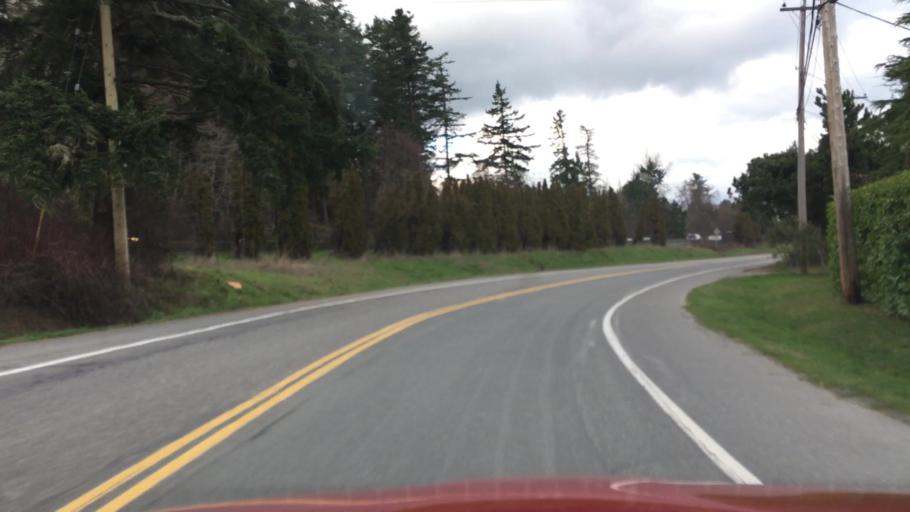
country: CA
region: British Columbia
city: North Saanich
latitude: 48.6009
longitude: -123.3960
